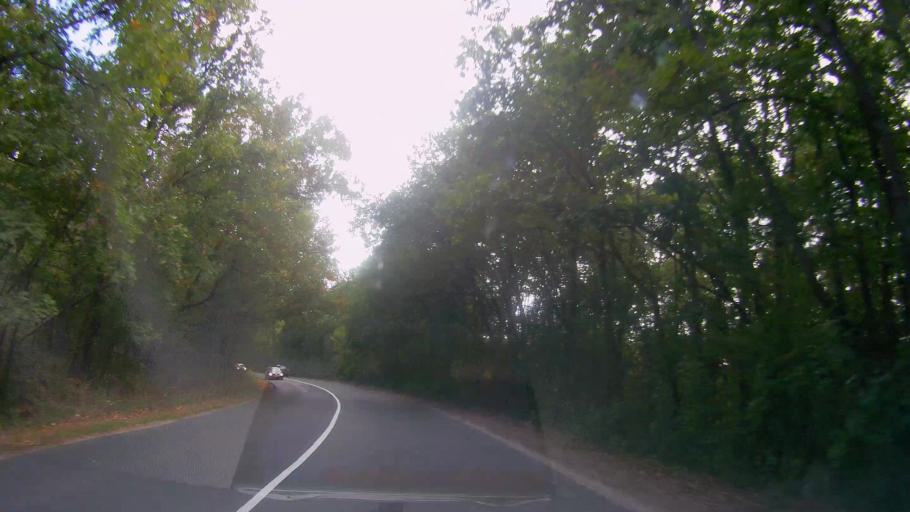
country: BG
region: Burgas
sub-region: Obshtina Primorsko
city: Primorsko
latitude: 42.2938
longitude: 27.7301
